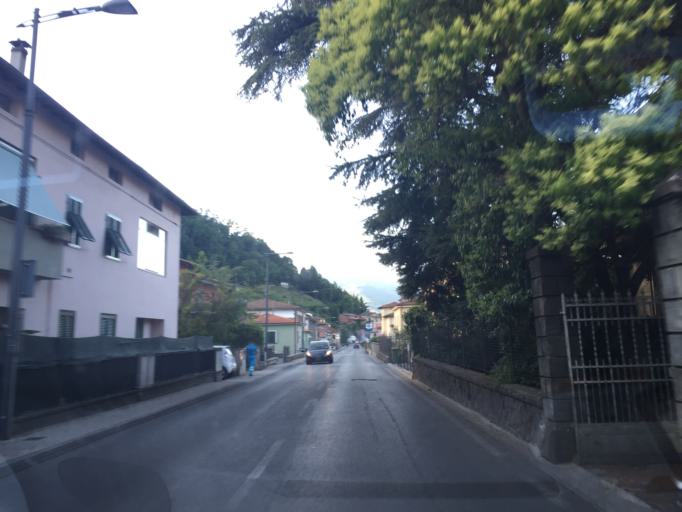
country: IT
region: Tuscany
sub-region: Provincia di Lucca
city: Castelnuovo di Garfagnana
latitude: 44.1047
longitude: 10.4072
